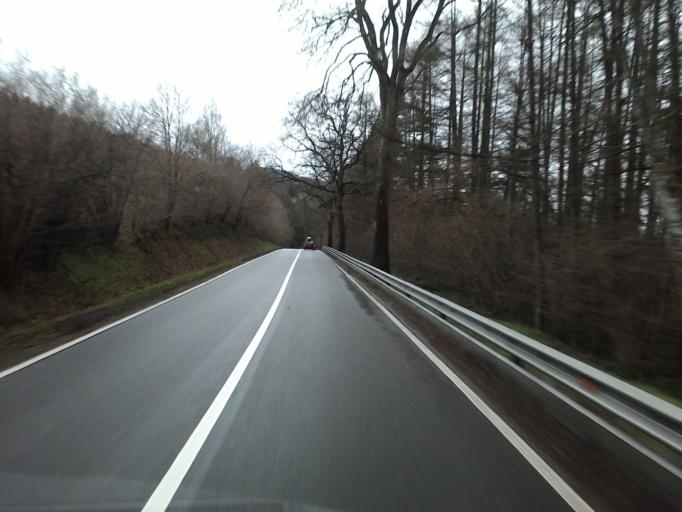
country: BE
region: Wallonia
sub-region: Province de Liege
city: Trois-Ponts
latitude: 50.3796
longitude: 5.8980
